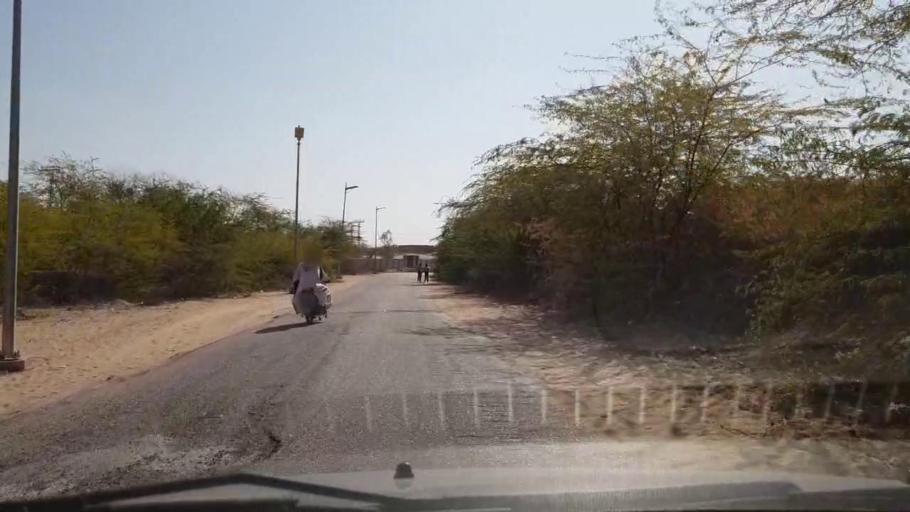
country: PK
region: Sindh
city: Diplo
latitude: 24.4749
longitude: 69.5807
